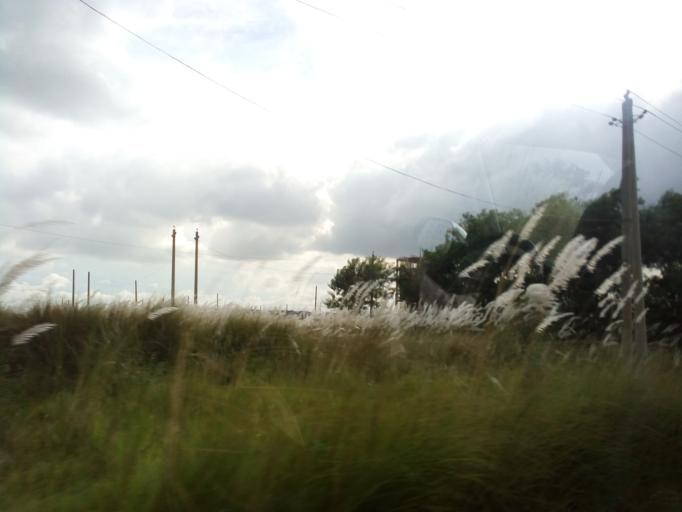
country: BD
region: Dhaka
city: Tungi
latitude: 23.8684
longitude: 90.3639
